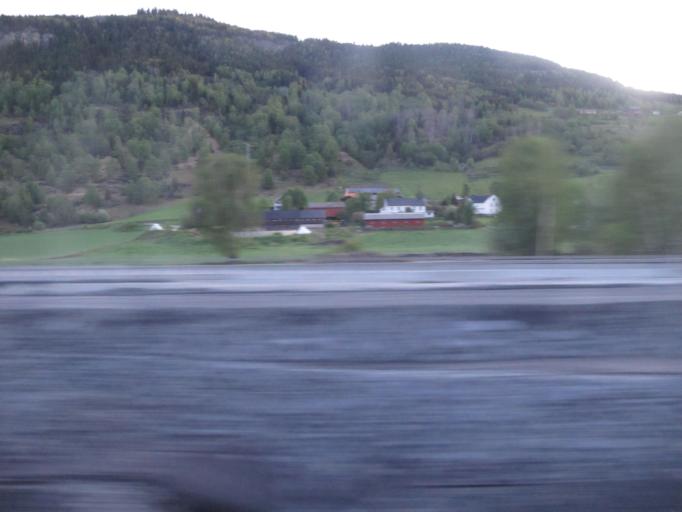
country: NO
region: Oppland
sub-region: Sor-Fron
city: Hundorp
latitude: 61.5478
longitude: 10.0303
